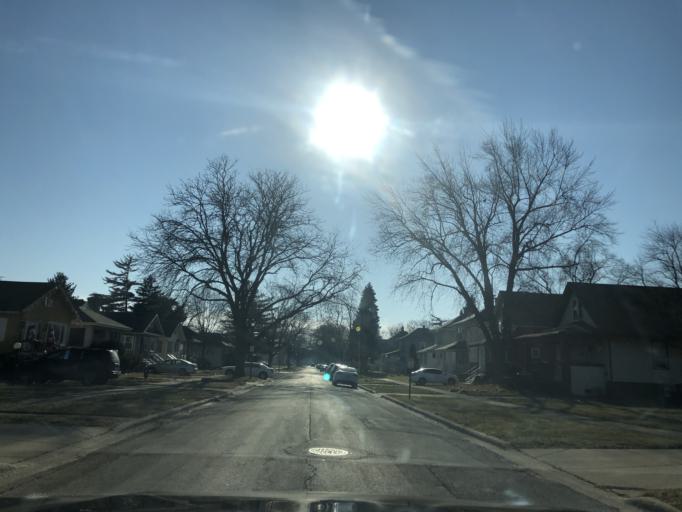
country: US
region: Illinois
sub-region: Cook County
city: Maywood
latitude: 41.8754
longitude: -87.8363
